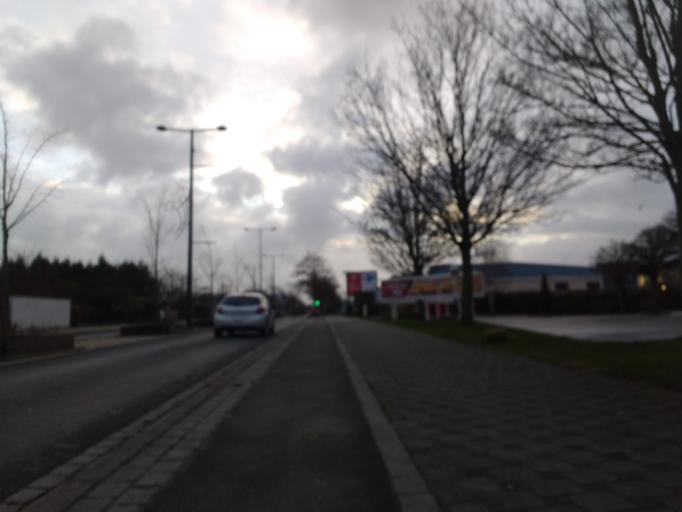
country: FR
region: Picardie
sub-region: Departement de la Somme
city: Longueau
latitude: 49.8683
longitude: 2.3629
